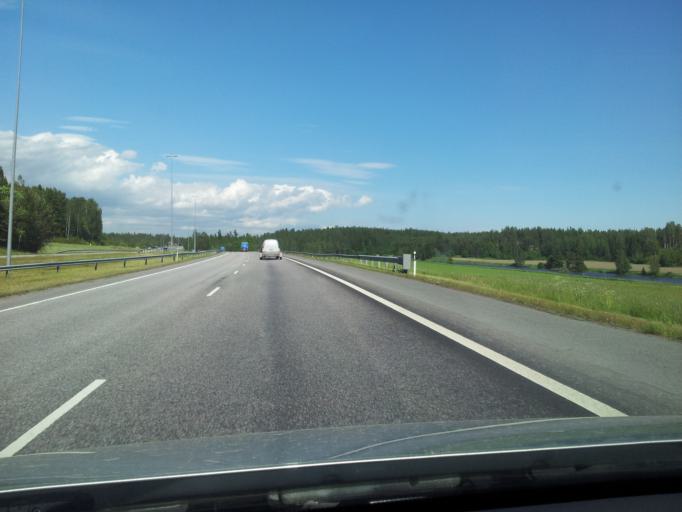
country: FI
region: Uusimaa
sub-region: Porvoo
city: Porvoo
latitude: 60.3604
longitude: 25.5437
